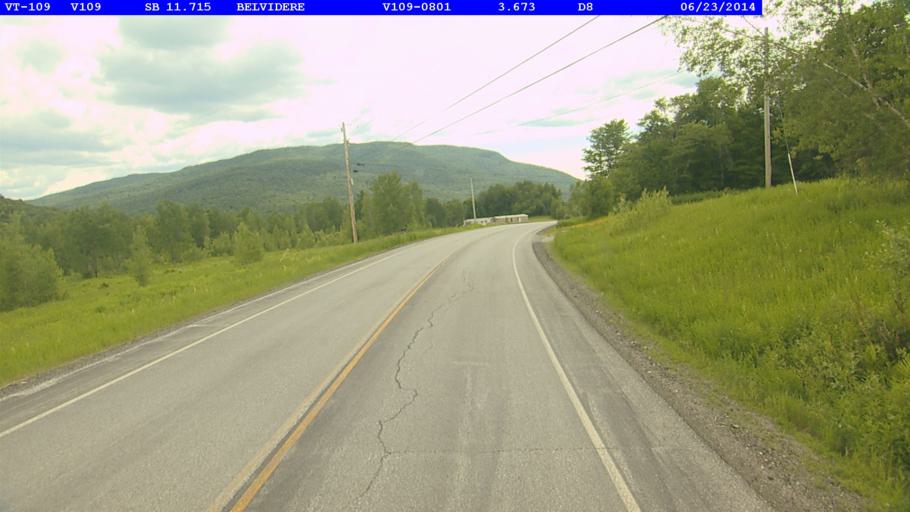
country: US
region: Vermont
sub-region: Lamoille County
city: Johnson
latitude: 44.7571
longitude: -72.6797
